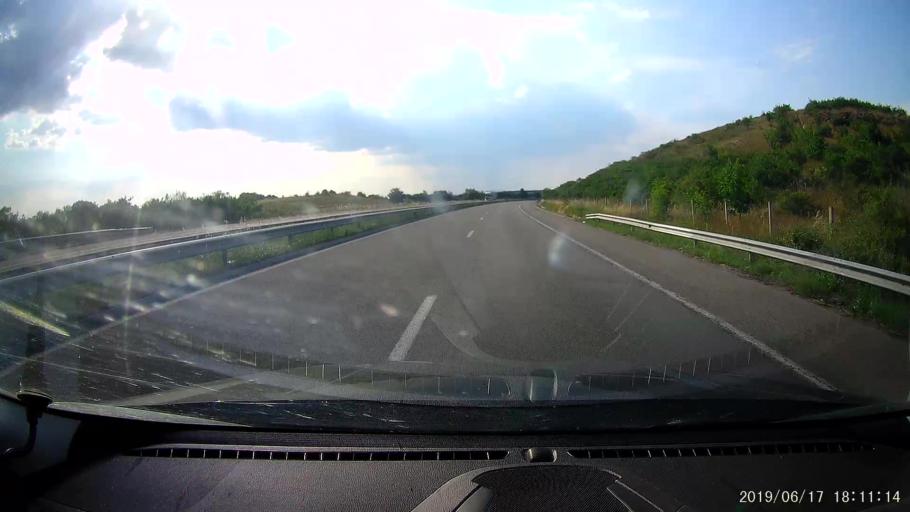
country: BG
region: Khaskovo
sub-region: Obshtina Lyubimets
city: Lyubimets
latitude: 41.8808
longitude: 26.0555
